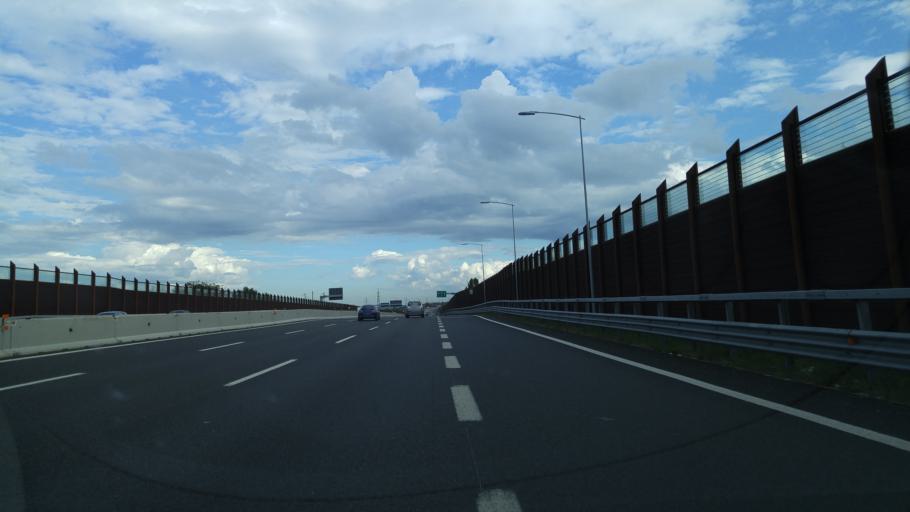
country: IT
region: Emilia-Romagna
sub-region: Provincia di Rimini
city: Rimini
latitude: 44.0340
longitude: 12.5711
